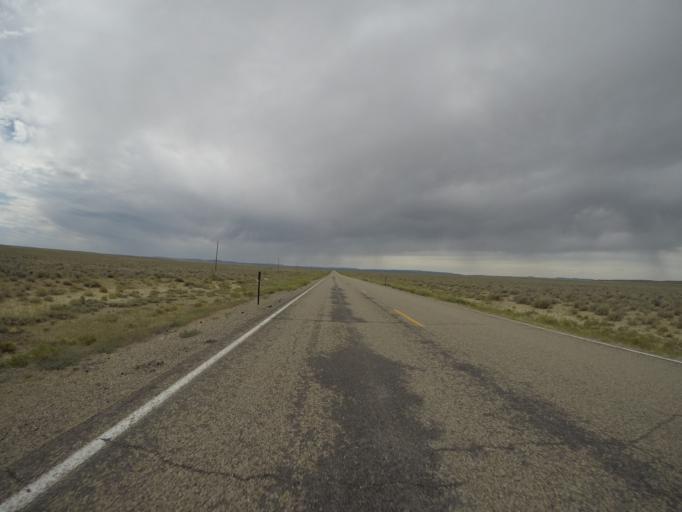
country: US
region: Wyoming
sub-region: Lincoln County
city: Kemmerer
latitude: 41.9627
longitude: -110.1148
